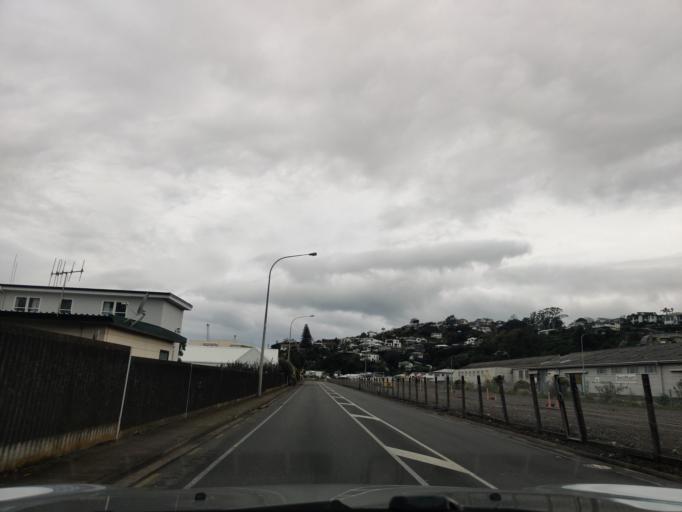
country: NZ
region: Hawke's Bay
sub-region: Napier City
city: Napier
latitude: -39.4798
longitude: 176.9041
